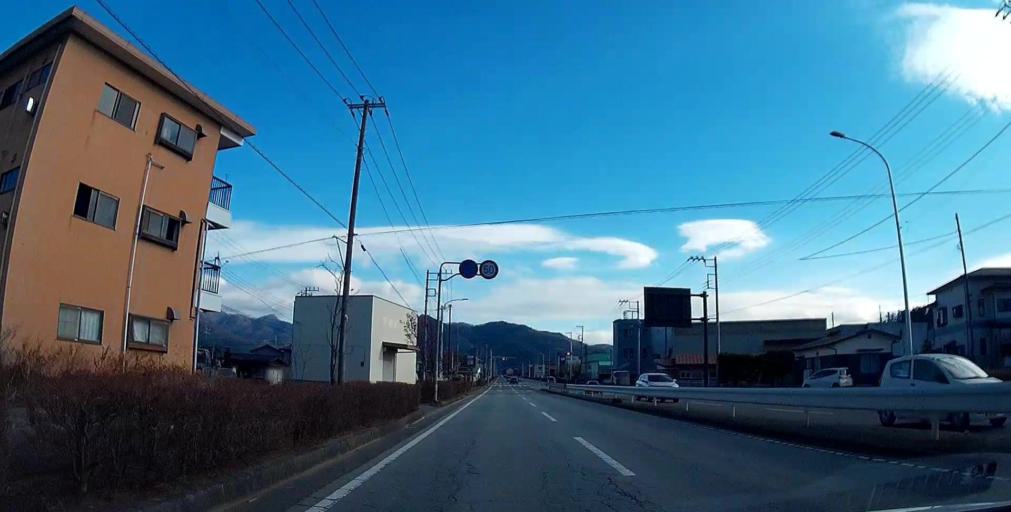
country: JP
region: Yamanashi
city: Fujikawaguchiko
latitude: 35.4897
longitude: 138.7953
